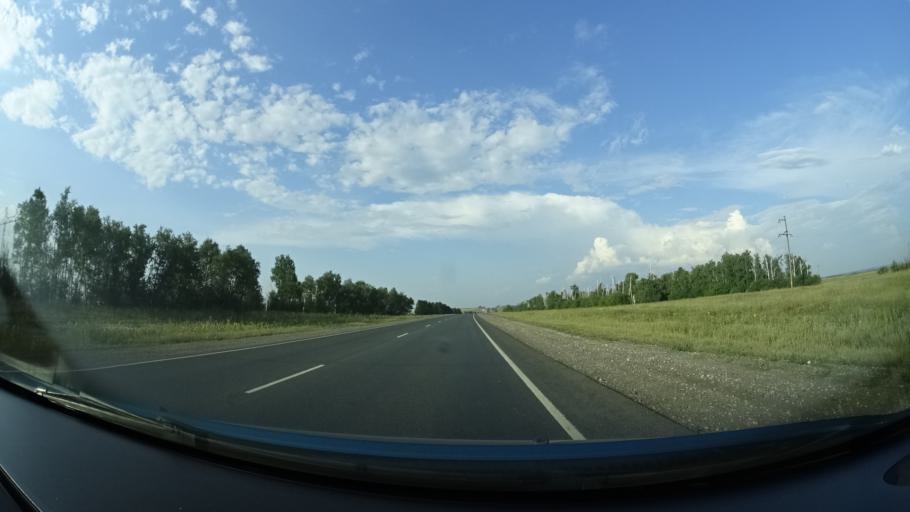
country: RU
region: Samara
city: Sukhodol
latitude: 53.7170
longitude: 50.8229
